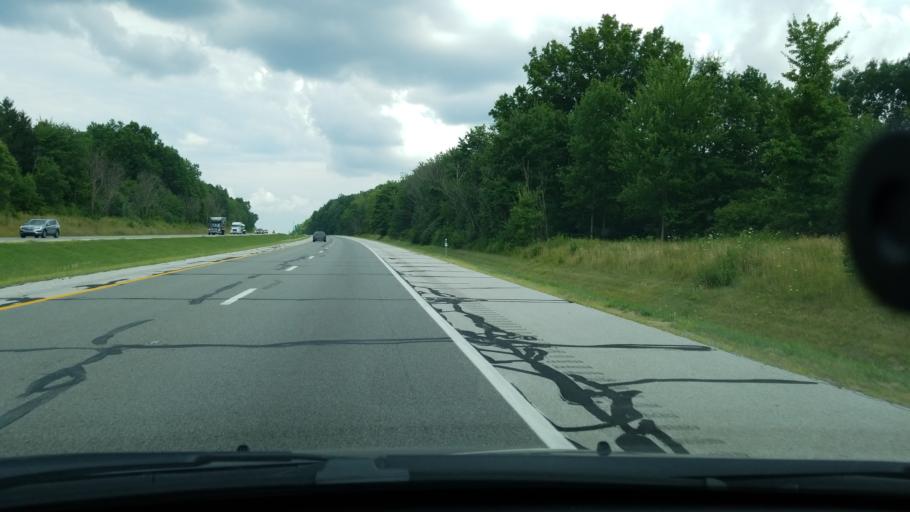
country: US
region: Ohio
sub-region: Mahoning County
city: Canfield
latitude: 41.0401
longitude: -80.7574
